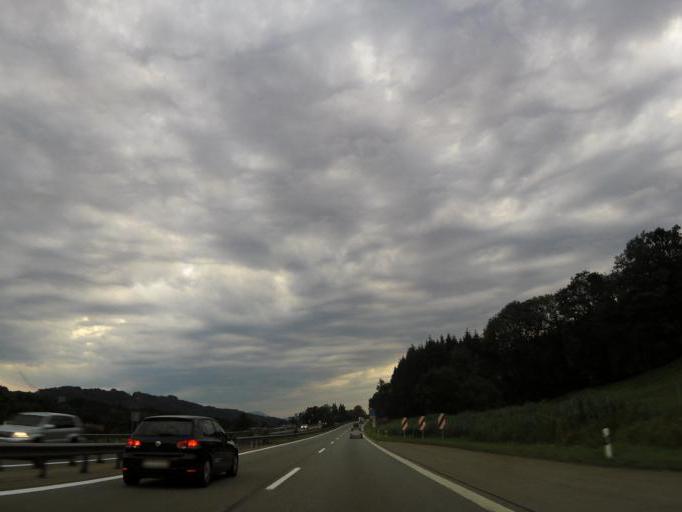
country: DE
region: Bavaria
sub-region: Upper Bavaria
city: Frasdorf
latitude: 47.7981
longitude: 12.2481
